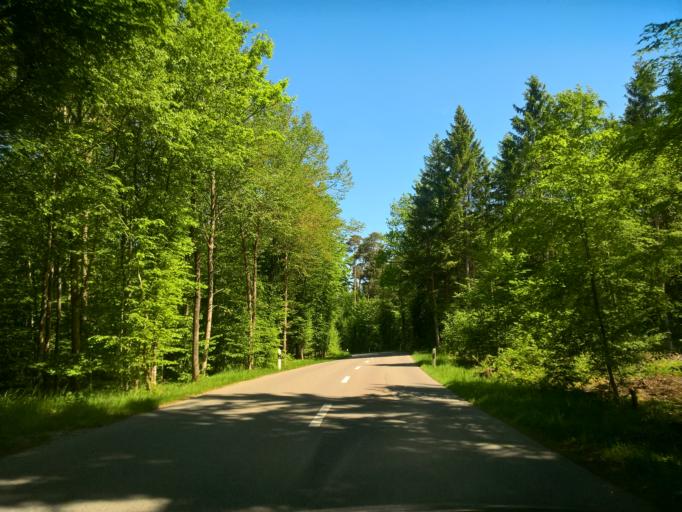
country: DE
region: Baden-Wuerttemberg
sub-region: Freiburg Region
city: Lottstetten
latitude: 47.6123
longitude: 8.6083
